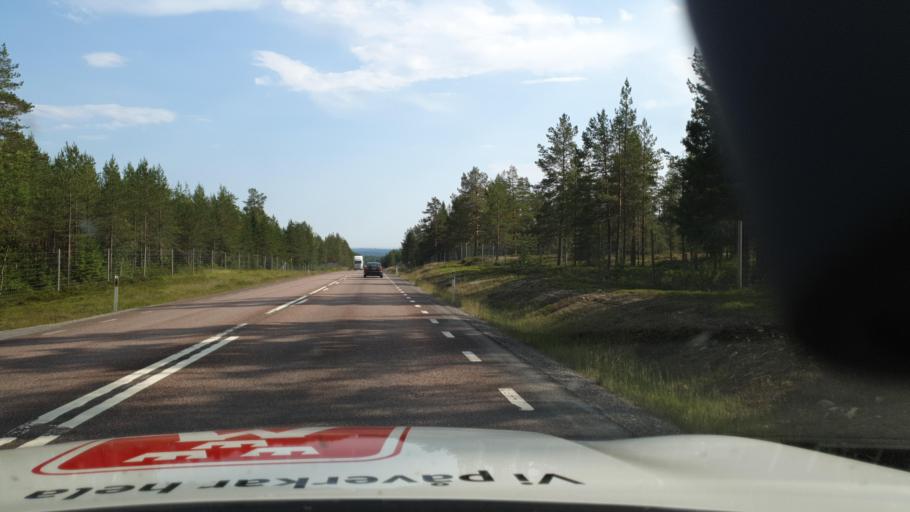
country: SE
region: Vaesterbotten
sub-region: Skelleftea Kommun
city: Burea
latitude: 64.4320
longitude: 21.2808
